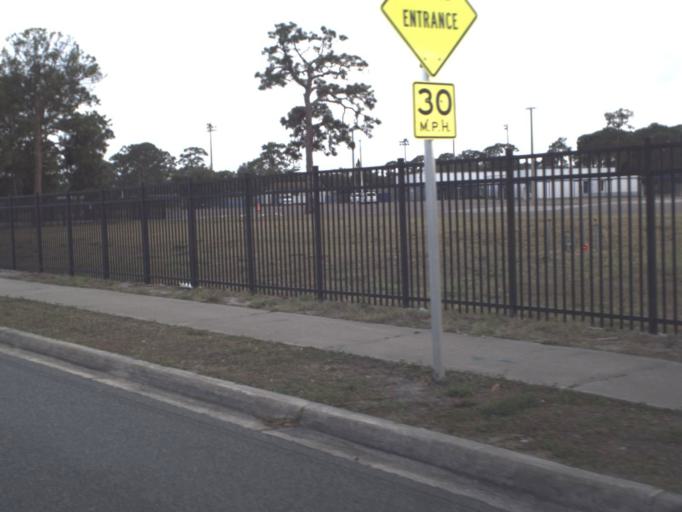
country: US
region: Florida
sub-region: Brevard County
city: Titusville
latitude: 28.5929
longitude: -80.8042
